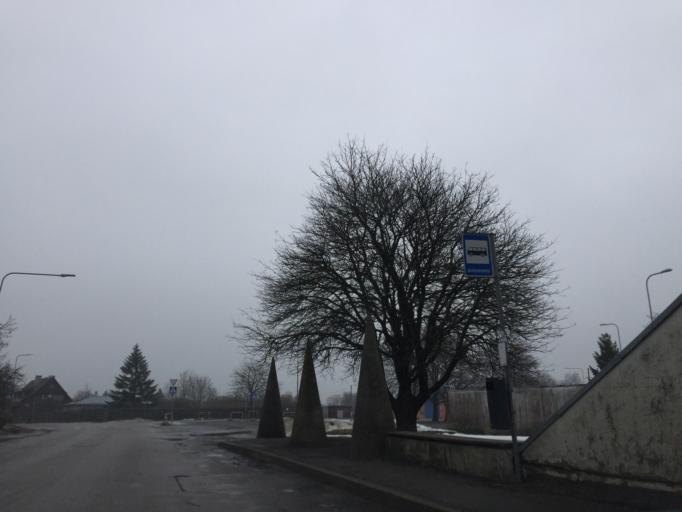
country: EE
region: Saare
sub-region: Kuressaare linn
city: Kuressaare
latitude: 58.2533
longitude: 22.5005
